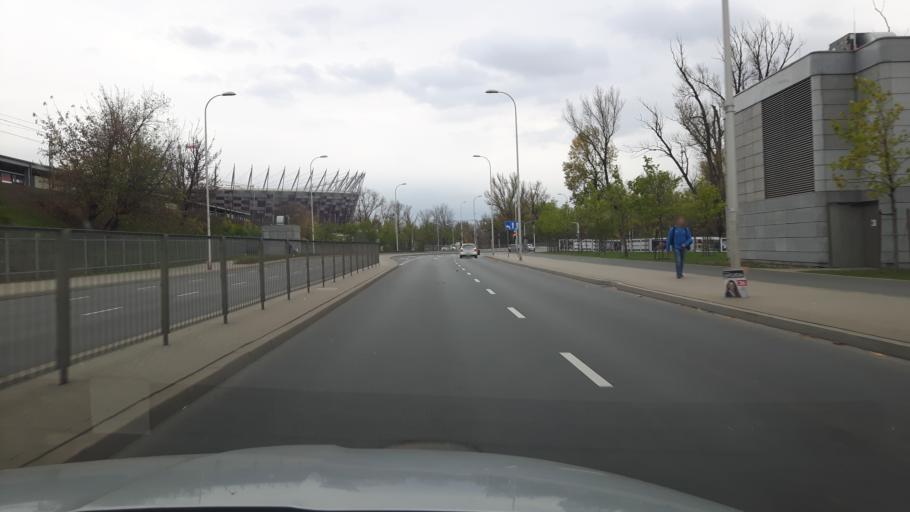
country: PL
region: Masovian Voivodeship
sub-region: Warszawa
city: Praga Polnoc
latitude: 52.2458
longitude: 21.0431
